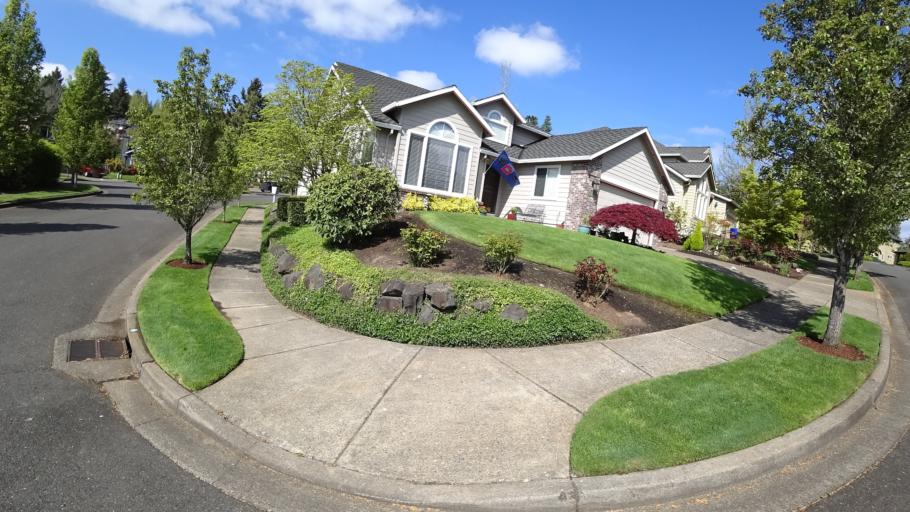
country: US
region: Oregon
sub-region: Washington County
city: King City
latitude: 45.4384
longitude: -122.8337
